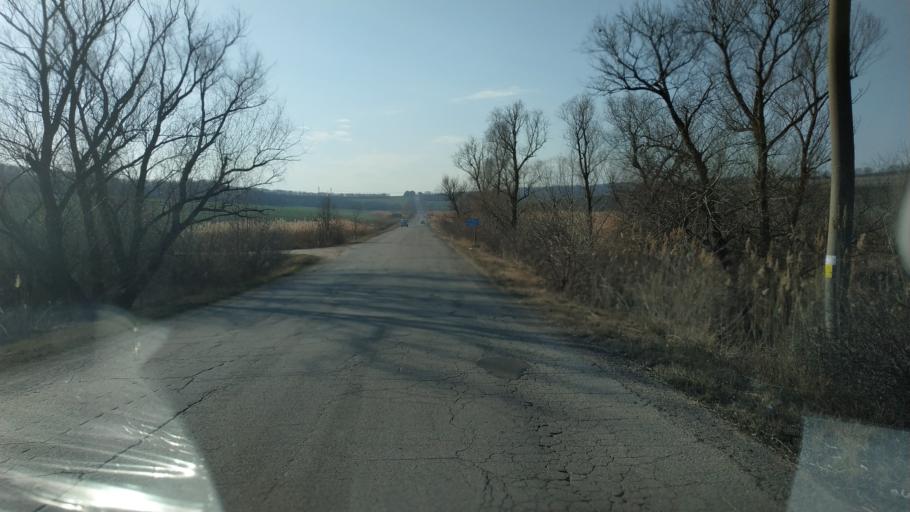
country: MD
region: Chisinau
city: Singera
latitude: 46.8872
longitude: 29.0391
